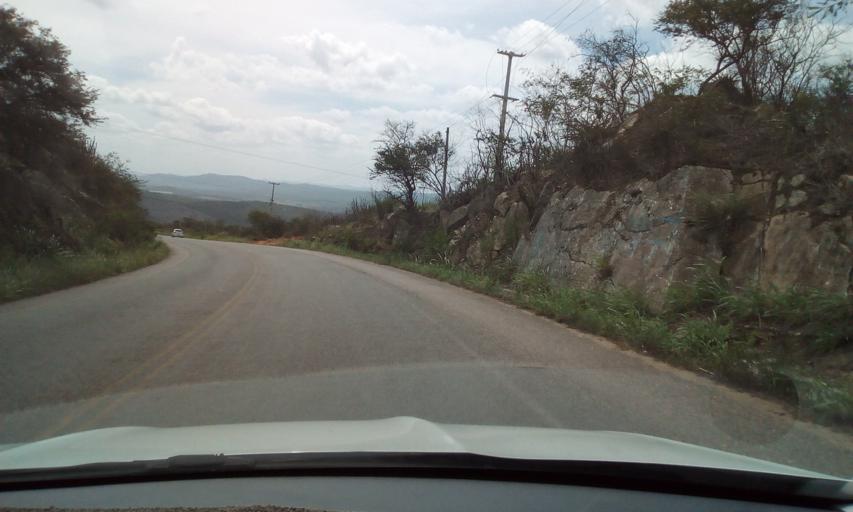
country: BR
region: Pernambuco
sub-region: Bezerros
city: Bezerros
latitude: -8.2739
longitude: -35.7443
